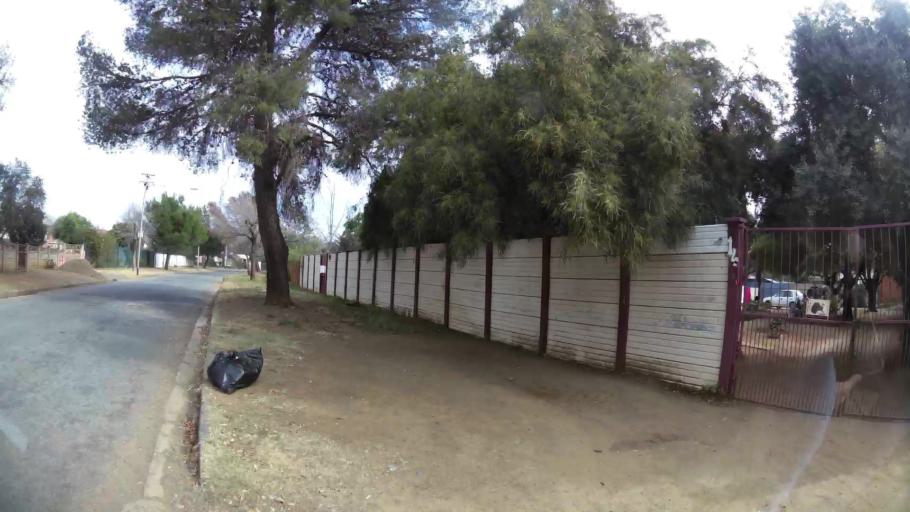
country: ZA
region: Orange Free State
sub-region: Mangaung Metropolitan Municipality
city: Bloemfontein
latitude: -29.1315
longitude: 26.1991
